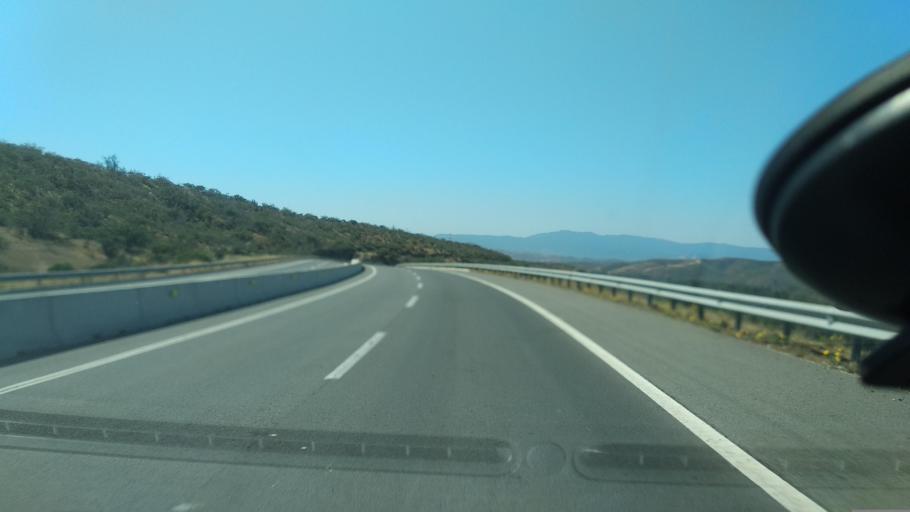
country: CL
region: Valparaiso
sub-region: Provincia de Marga Marga
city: Villa Alemana
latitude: -33.0401
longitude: -71.3188
